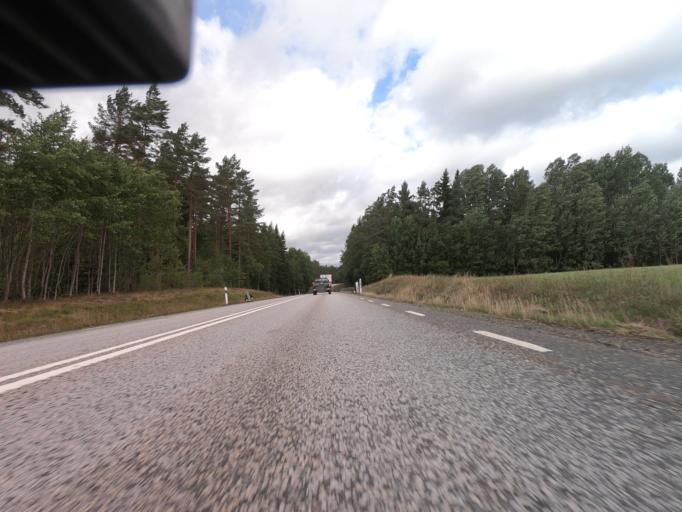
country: SE
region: Joenkoeping
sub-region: Vaggeryds Kommun
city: Vaggeryd
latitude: 57.5674
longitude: 14.2427
